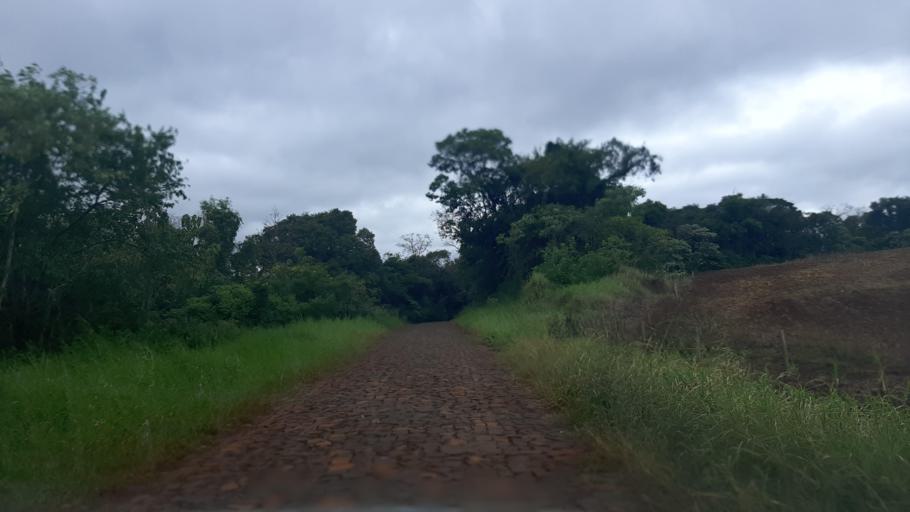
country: BR
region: Parana
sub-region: Ampere
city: Ampere
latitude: -26.0378
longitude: -53.5136
